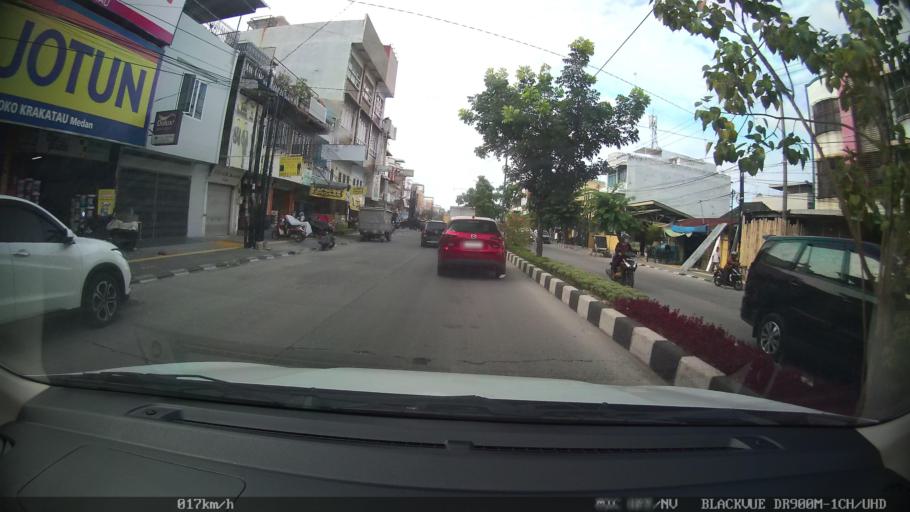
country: ID
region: North Sumatra
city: Medan
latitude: 3.6130
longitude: 98.6806
